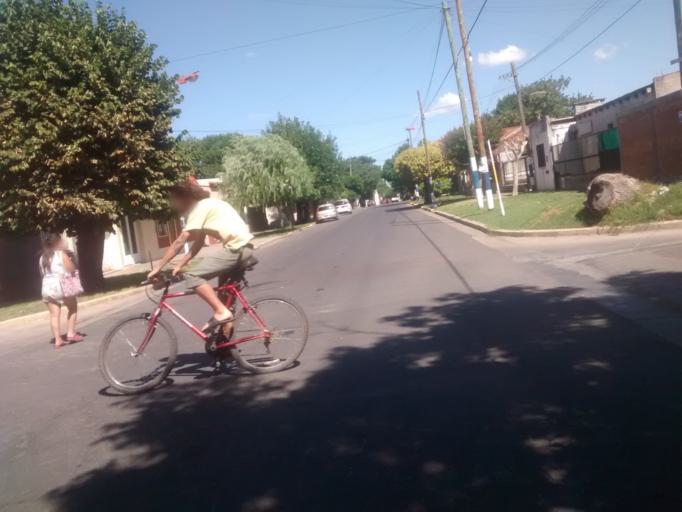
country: AR
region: Buenos Aires
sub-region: Partido de La Plata
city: La Plata
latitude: -34.9369
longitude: -57.9224
